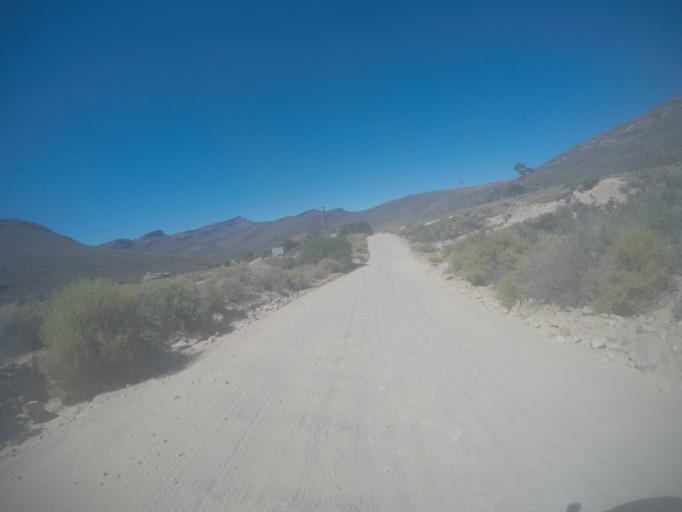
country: ZA
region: Western Cape
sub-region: West Coast District Municipality
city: Clanwilliam
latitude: -32.5493
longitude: 19.3607
